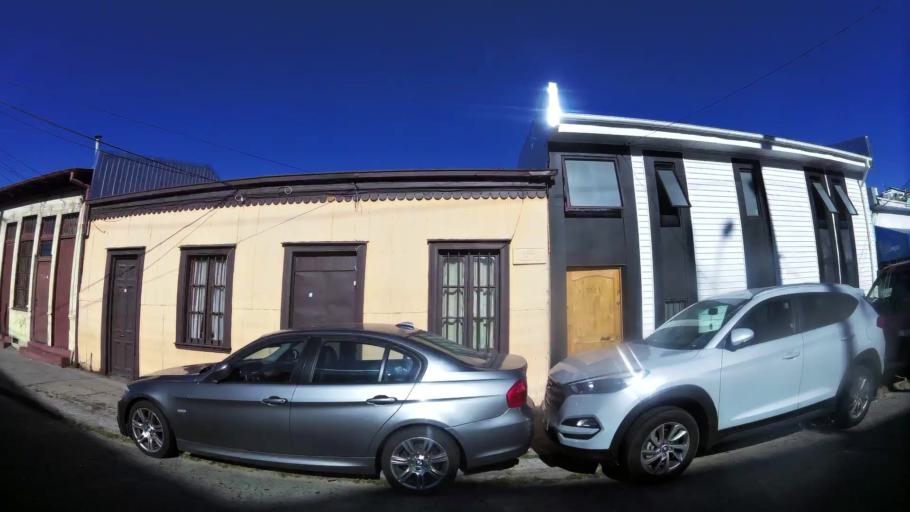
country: CL
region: Valparaiso
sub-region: Provincia de Valparaiso
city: Valparaiso
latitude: -33.0531
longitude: -71.6175
